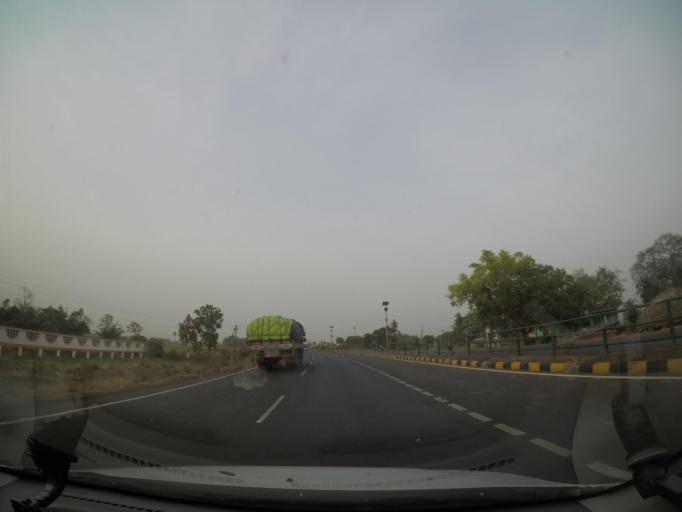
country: IN
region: Andhra Pradesh
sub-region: Krishna
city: Gannavaram
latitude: 16.6150
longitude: 80.9239
